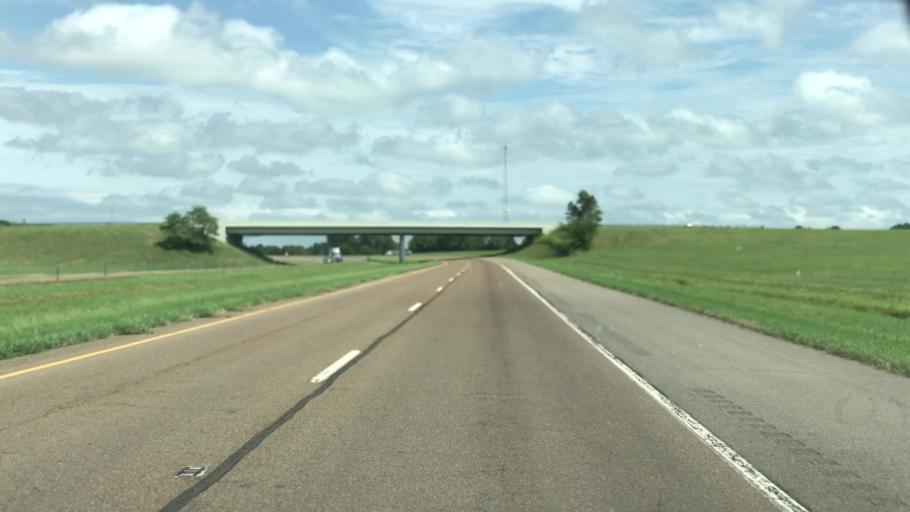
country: US
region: Tennessee
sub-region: Obion County
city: Union City
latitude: 36.4436
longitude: -89.0147
